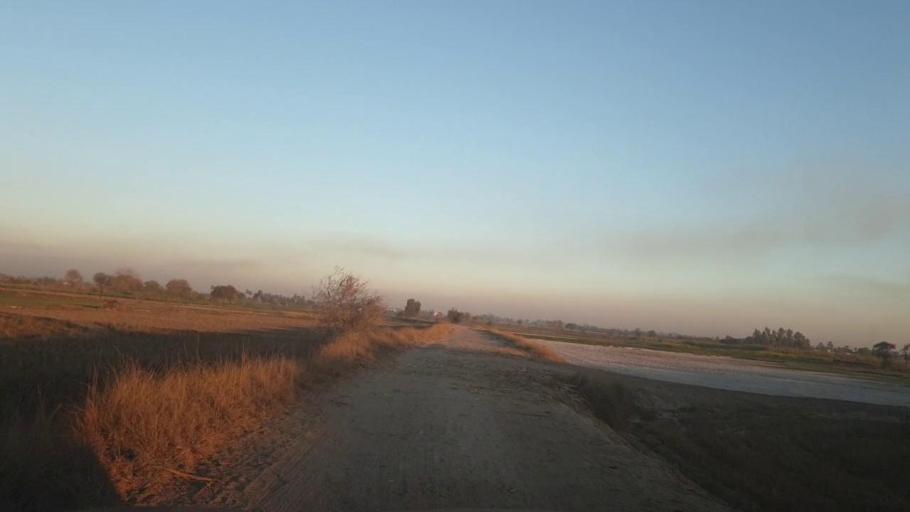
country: PK
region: Sindh
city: Ghotki
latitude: 28.0348
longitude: 69.3005
